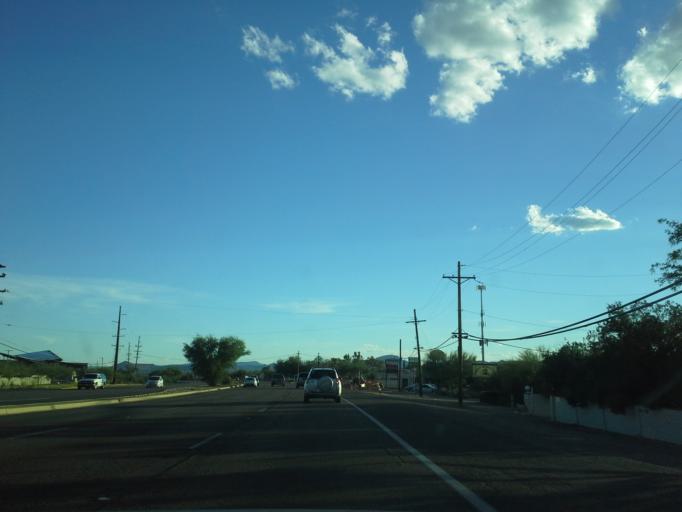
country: US
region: Arizona
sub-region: Pima County
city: Casas Adobes
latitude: 32.3142
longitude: -110.9776
